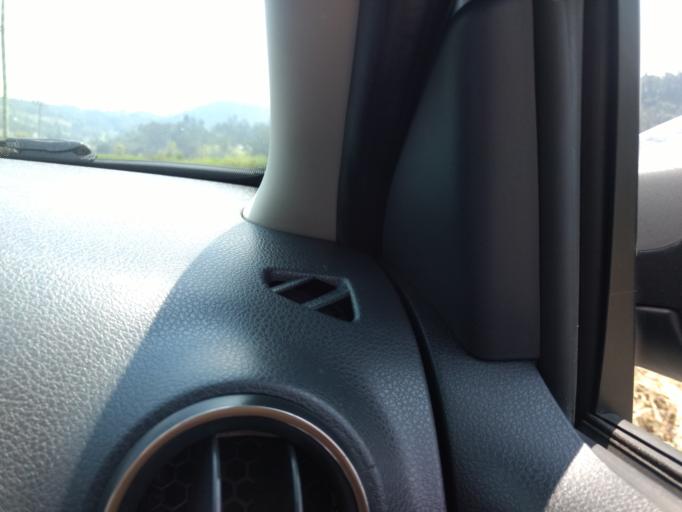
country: CO
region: Boyaca
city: Raquira
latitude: 5.4969
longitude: -73.7107
